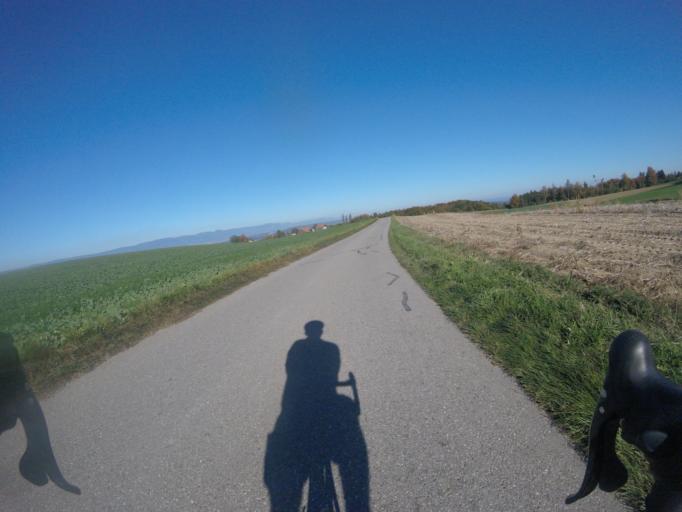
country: CH
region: Bern
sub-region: Seeland District
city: Seedorf
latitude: 47.0268
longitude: 7.3386
